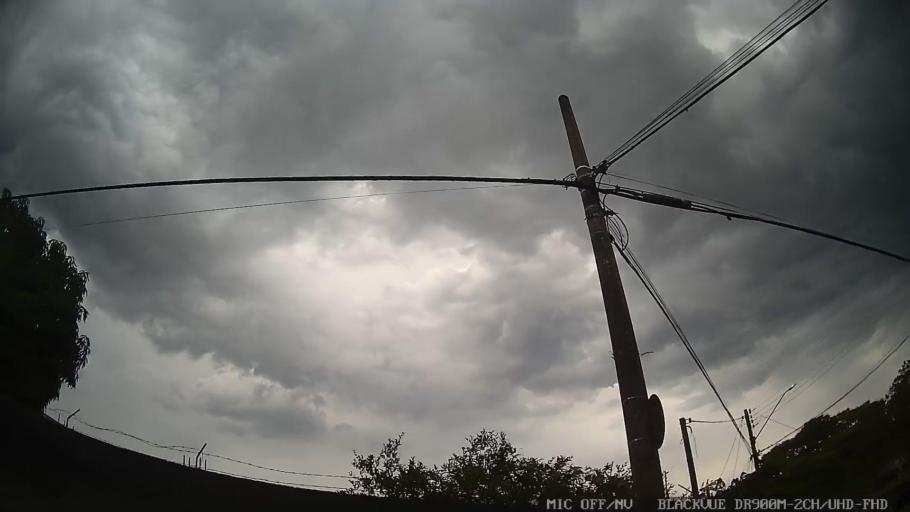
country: BR
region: Sao Paulo
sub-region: Itatiba
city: Itatiba
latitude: -23.0092
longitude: -46.8577
